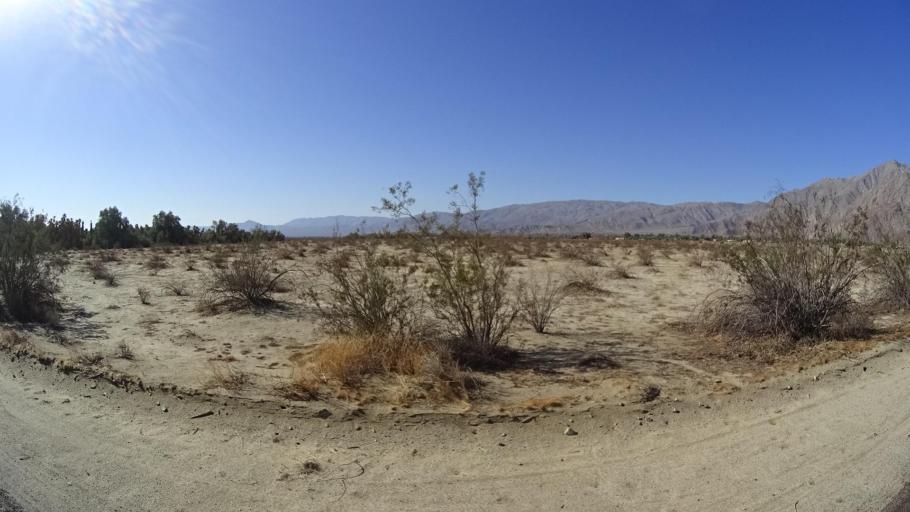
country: US
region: California
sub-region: San Diego County
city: Borrego Springs
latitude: 33.3015
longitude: -116.3770
